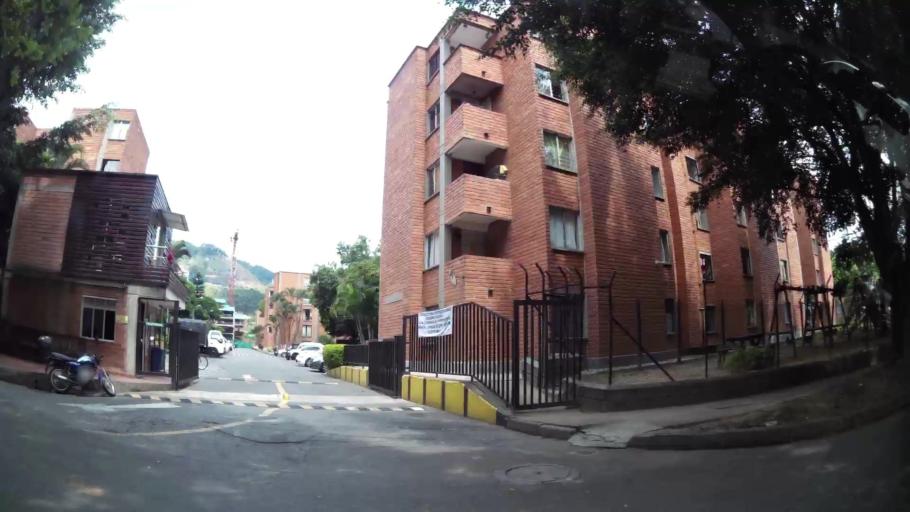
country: CO
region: Antioquia
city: Itagui
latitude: 6.1955
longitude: -75.5940
